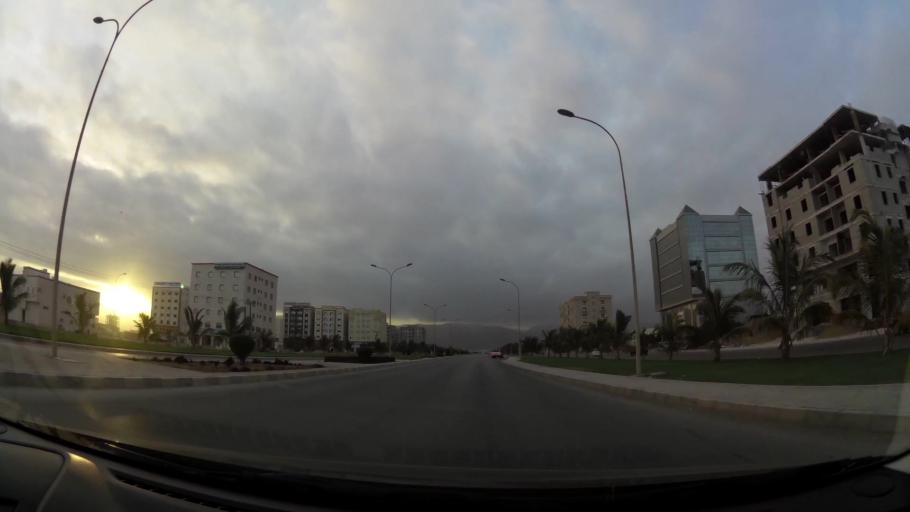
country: OM
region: Zufar
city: Salalah
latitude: 17.0224
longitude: 54.0336
